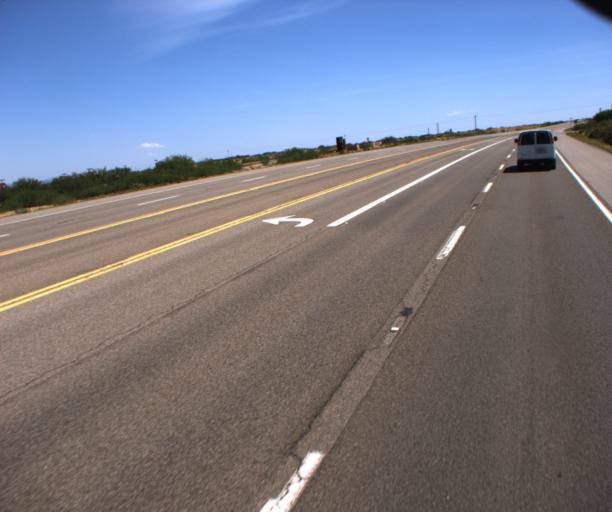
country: US
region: Arizona
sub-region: Cochise County
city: Whetstone
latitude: 31.9531
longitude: -110.3423
